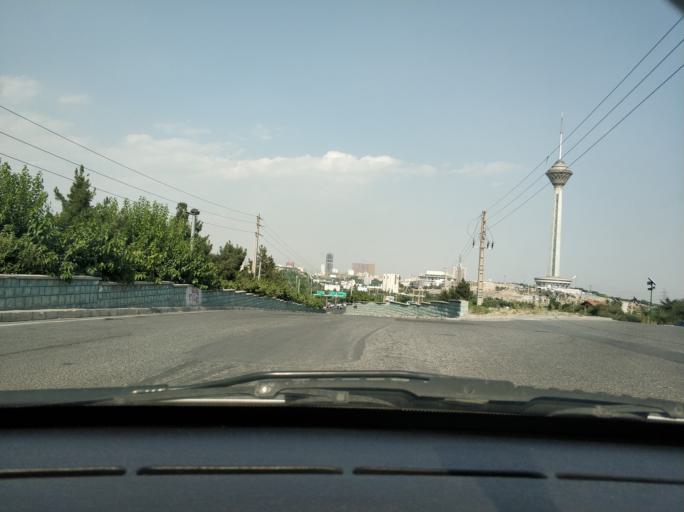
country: IR
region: Tehran
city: Tehran
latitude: 35.7492
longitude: 51.3608
